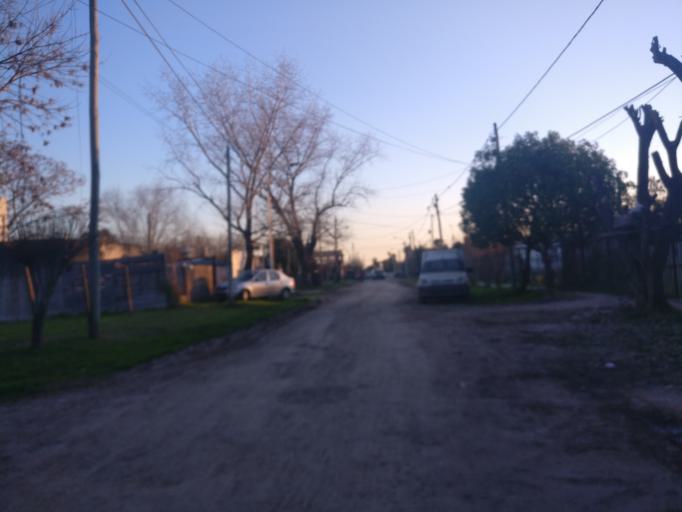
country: AR
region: Buenos Aires
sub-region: Partido de Ezeiza
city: Ezeiza
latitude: -34.9437
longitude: -58.6117
